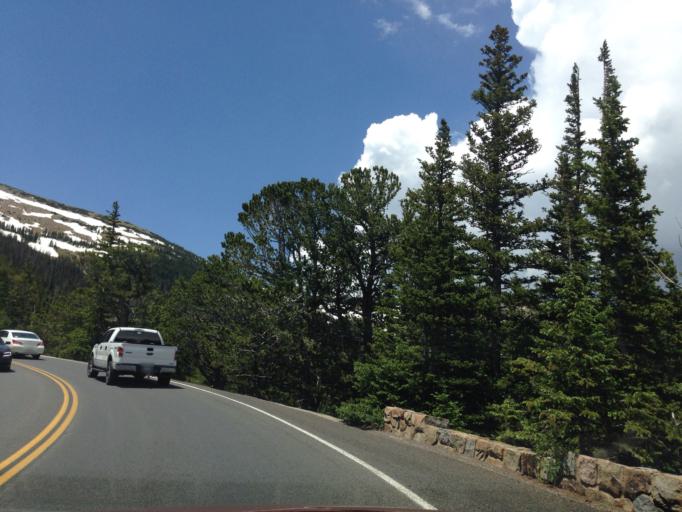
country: US
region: Colorado
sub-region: Larimer County
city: Estes Park
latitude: 40.3868
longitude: -105.6593
